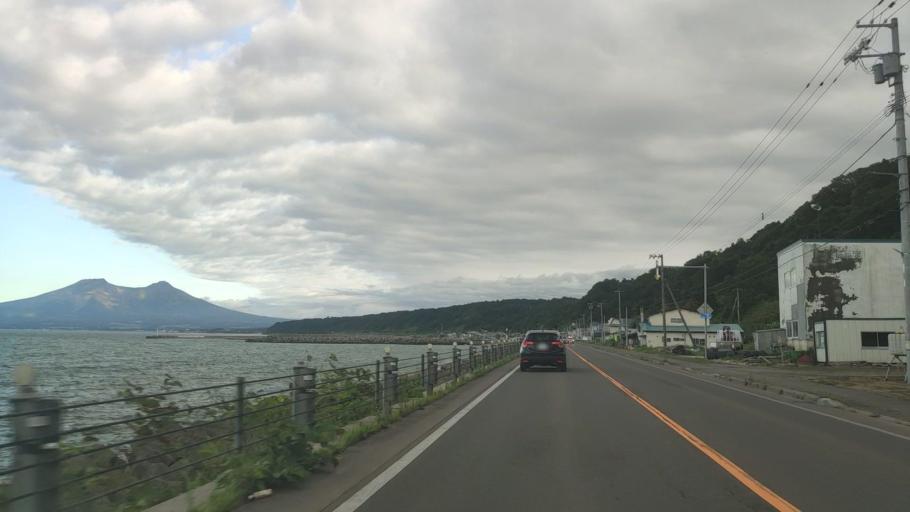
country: JP
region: Hokkaido
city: Nanae
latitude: 42.1392
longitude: 140.5048
